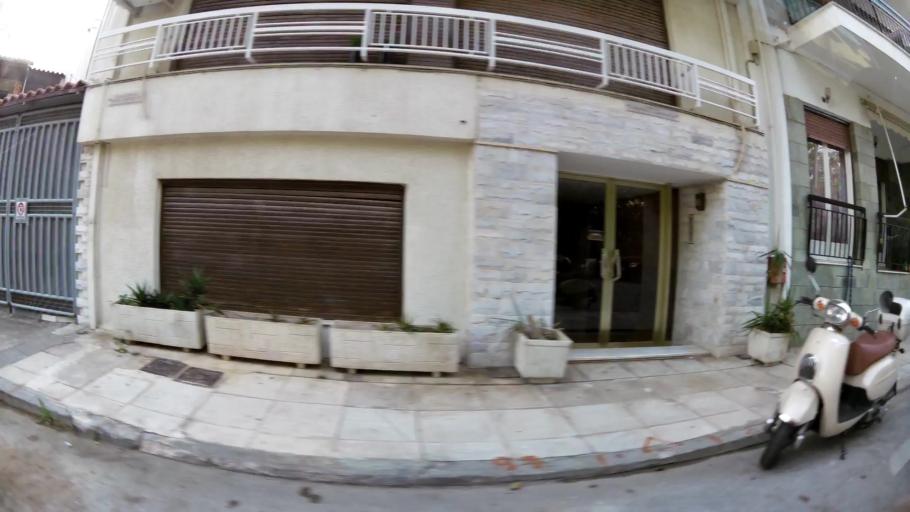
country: GR
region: Attica
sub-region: Nomarchia Athinas
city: Dhafni
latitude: 37.9487
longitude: 23.7276
